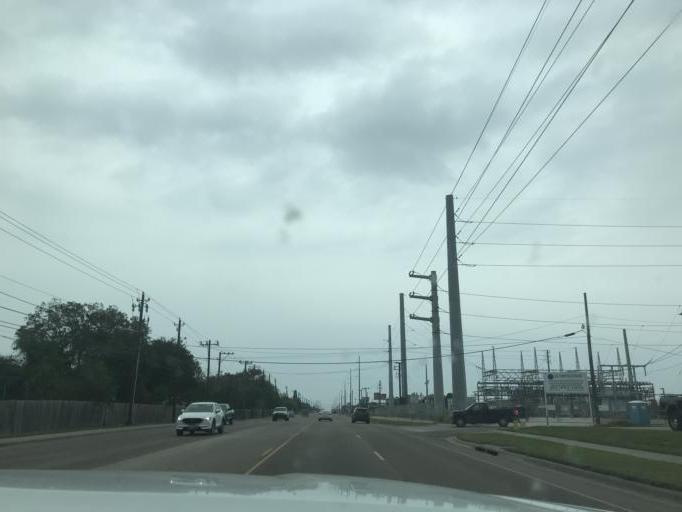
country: US
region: Texas
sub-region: Nueces County
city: Corpus Christi
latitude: 27.6972
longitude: -97.3738
